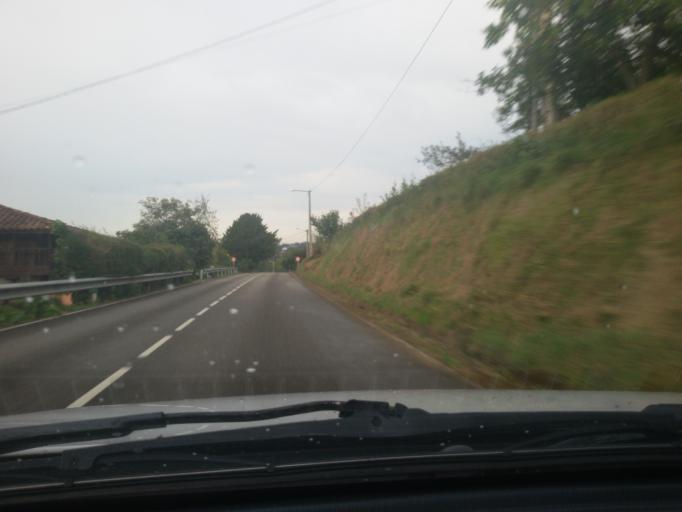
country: ES
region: Asturias
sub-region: Province of Asturias
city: Norena
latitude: 43.3678
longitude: -5.7435
